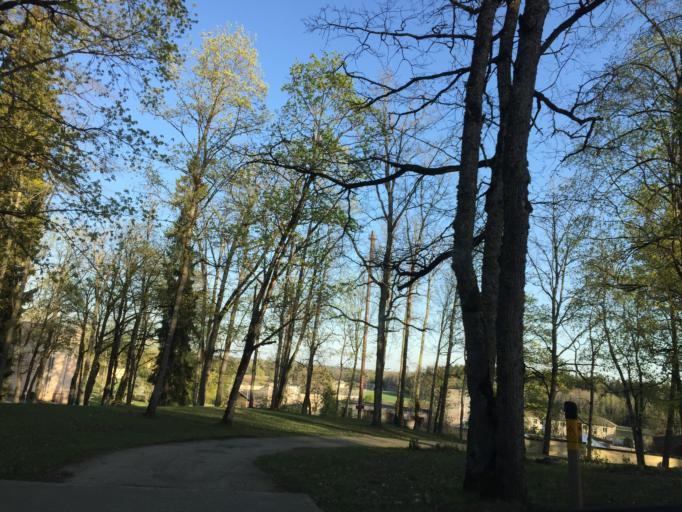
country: LV
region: Koknese
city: Koknese
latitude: 56.7228
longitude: 25.4828
